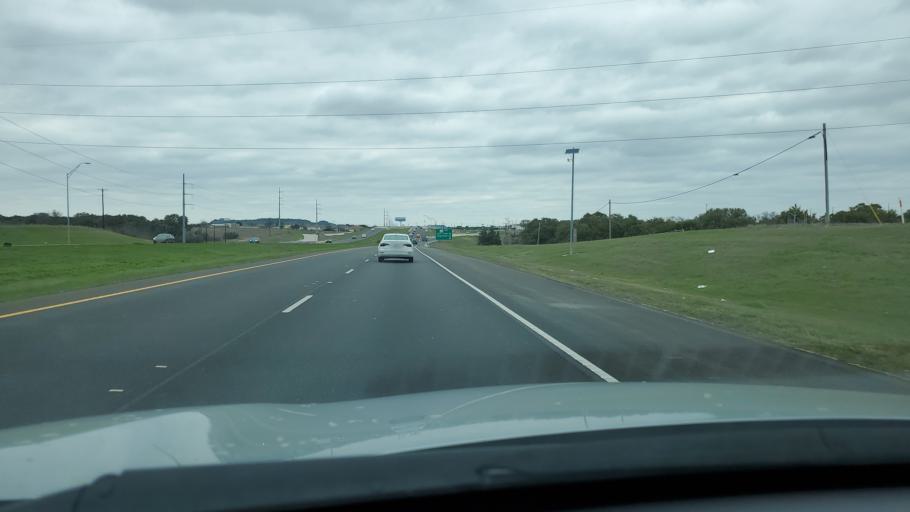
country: US
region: Texas
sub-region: Bell County
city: Killeen
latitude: 31.0513
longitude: -97.7632
